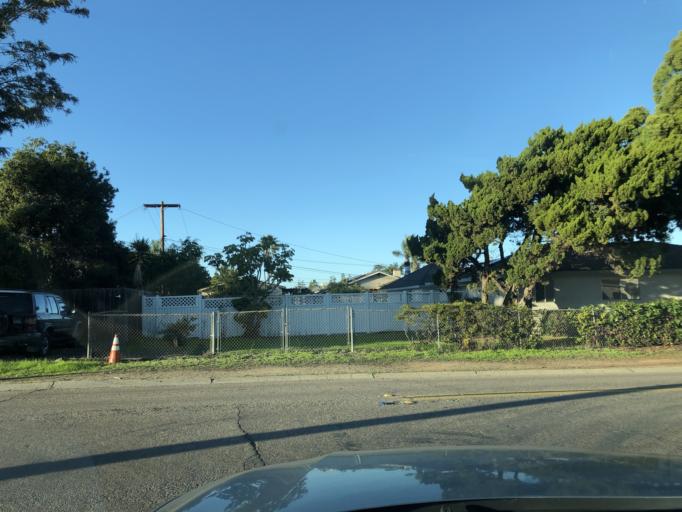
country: US
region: California
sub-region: San Diego County
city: Chula Vista
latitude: 32.6544
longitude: -117.0600
